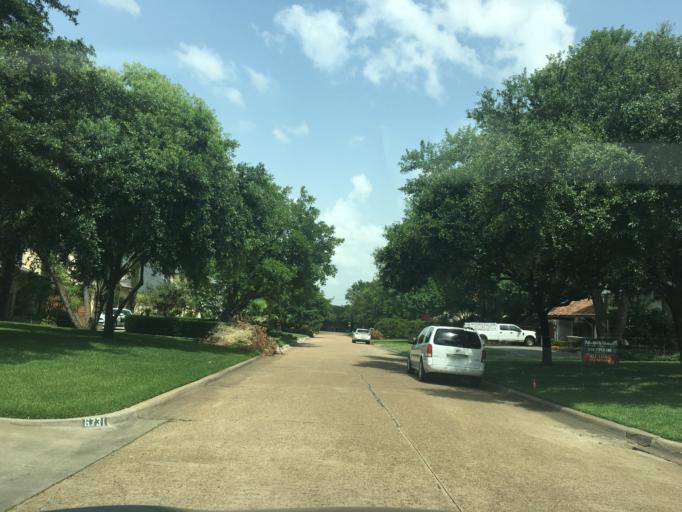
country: US
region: Texas
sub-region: Dallas County
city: University Park
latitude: 32.8883
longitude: -96.7890
